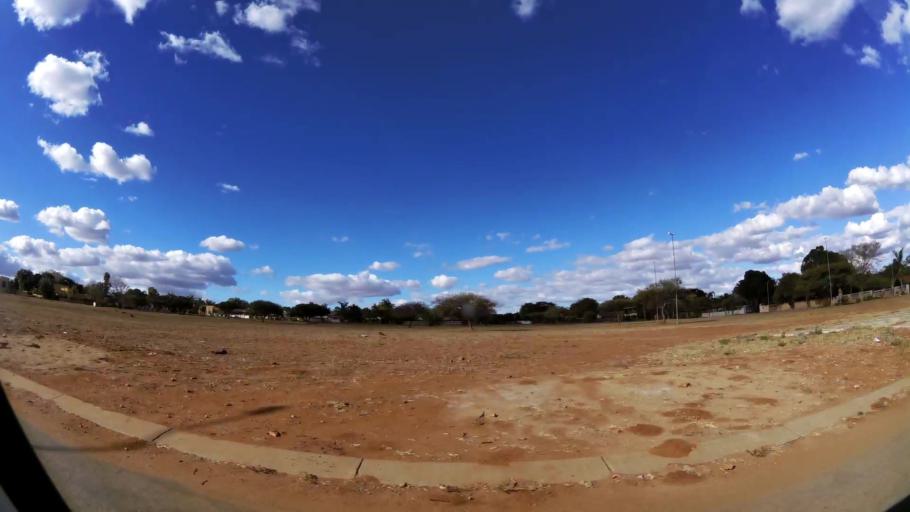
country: ZA
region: Limpopo
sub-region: Capricorn District Municipality
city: Polokwane
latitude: -23.9040
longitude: 29.4954
